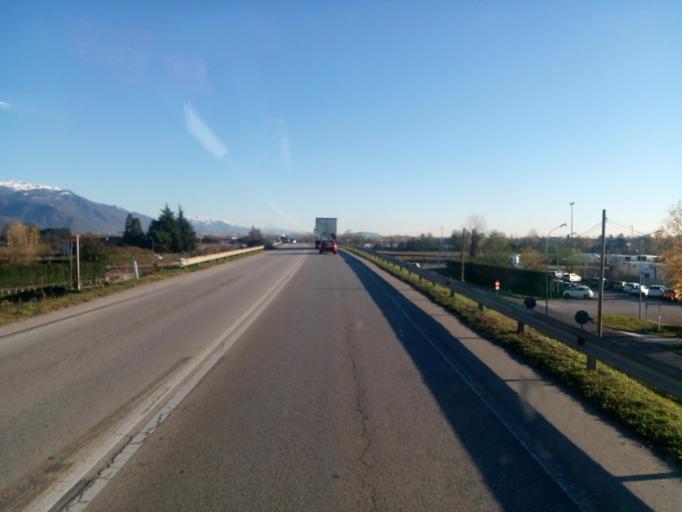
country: IT
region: Veneto
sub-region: Provincia di Vicenza
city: Nove
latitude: 45.7285
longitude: 11.6637
